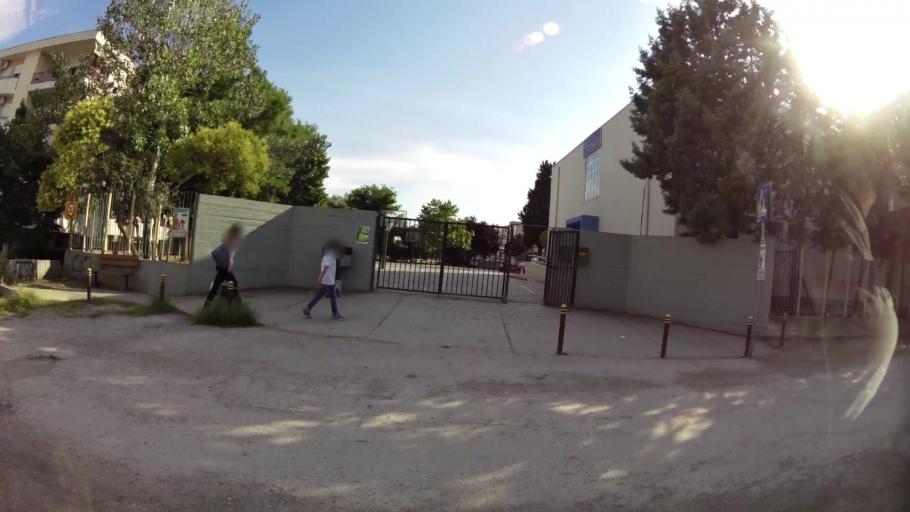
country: GR
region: Central Macedonia
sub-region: Nomos Thessalonikis
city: Kalamaria
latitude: 40.5704
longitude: 22.9632
